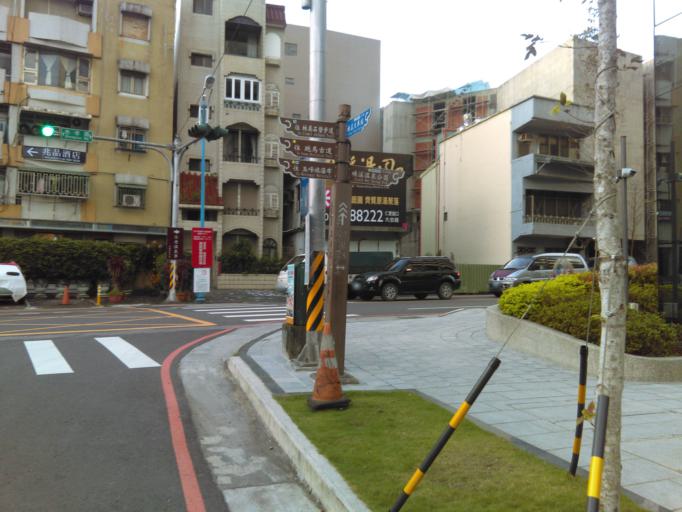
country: TW
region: Taiwan
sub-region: Yilan
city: Yilan
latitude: 24.8301
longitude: 121.7723
